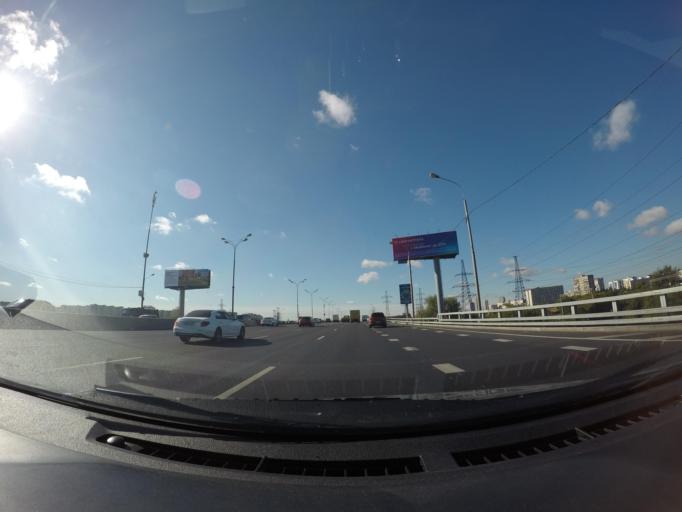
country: RU
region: Moscow
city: Zhulebino
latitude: 55.7108
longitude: 37.8363
